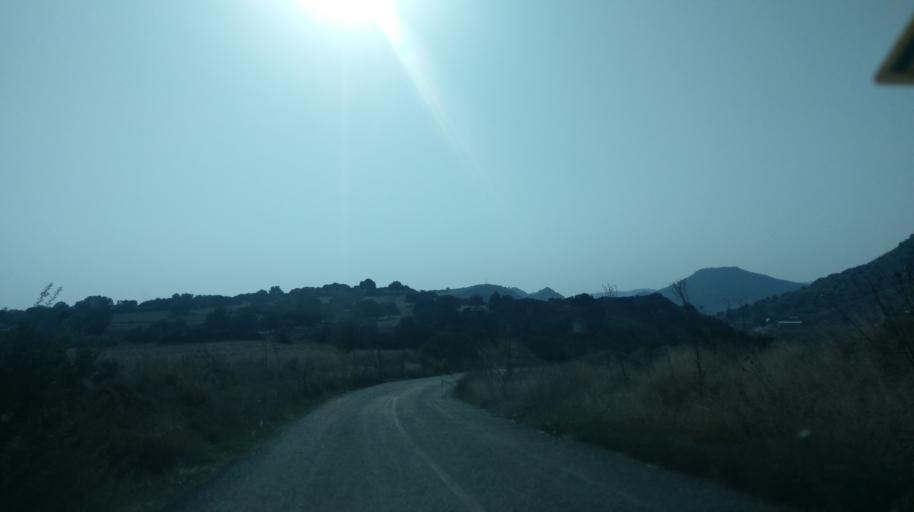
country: CY
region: Ammochostos
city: Rizokarpaso
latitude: 35.5200
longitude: 34.3178
